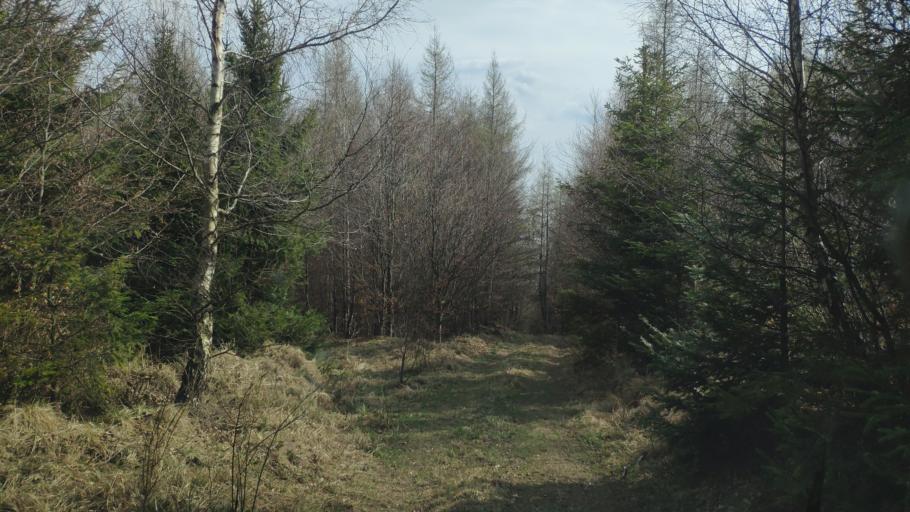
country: SK
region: Kosicky
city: Moldava nad Bodvou
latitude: 48.7390
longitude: 21.0484
